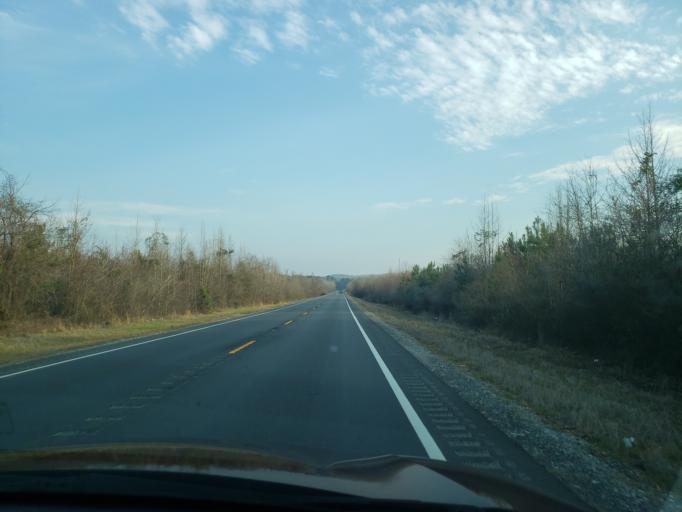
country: US
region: Alabama
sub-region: Hale County
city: Greensboro
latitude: 32.8340
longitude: -87.6061
